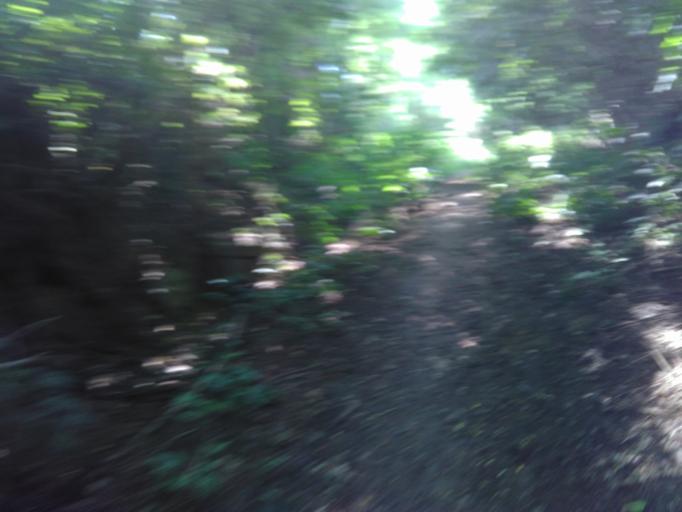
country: BE
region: Flanders
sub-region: Provincie Vlaams-Brabant
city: Herent
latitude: 50.8986
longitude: 4.6596
